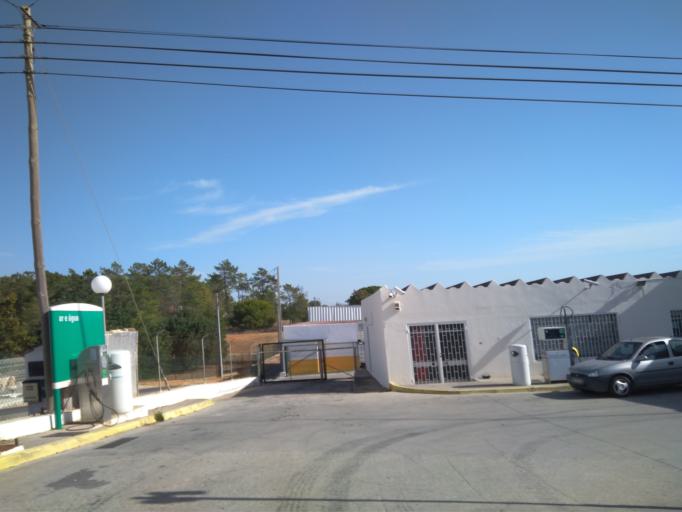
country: PT
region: Faro
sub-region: Faro
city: Santa Barbara de Nexe
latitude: 37.0832
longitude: -7.9586
